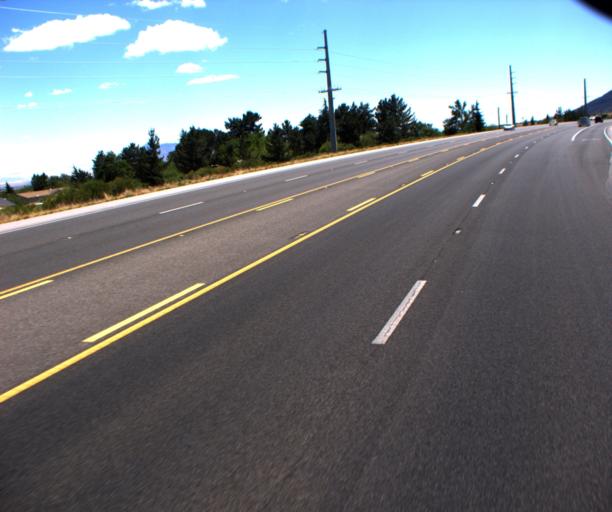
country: US
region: Arizona
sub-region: Cochise County
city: Sierra Vista Southeast
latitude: 31.4307
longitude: -110.2413
